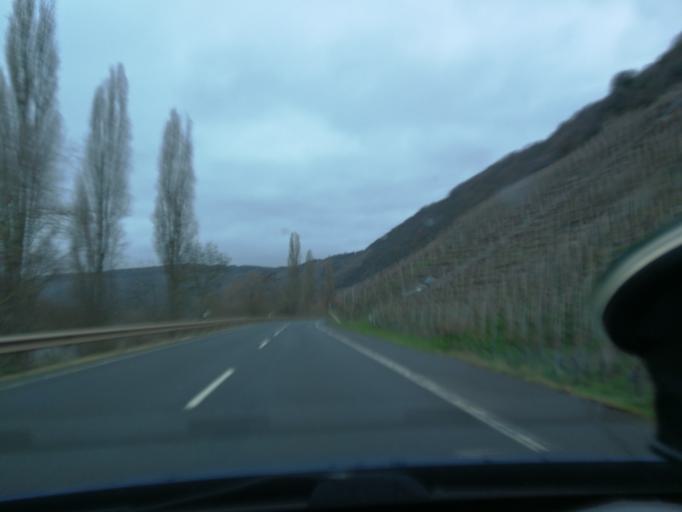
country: DE
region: Rheinland-Pfalz
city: Kowerich
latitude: 49.8308
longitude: 6.8838
